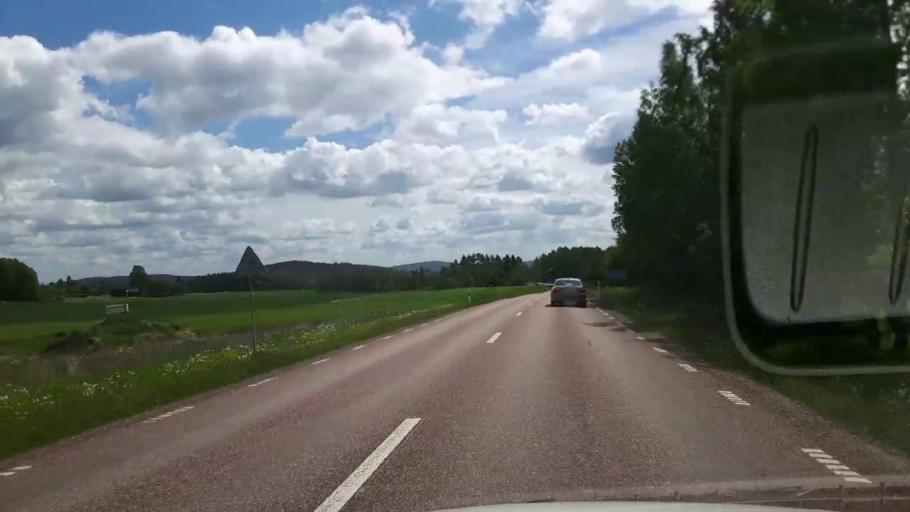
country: SE
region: Dalarna
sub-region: Saters Kommun
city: Saeter
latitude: 60.4261
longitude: 15.8376
